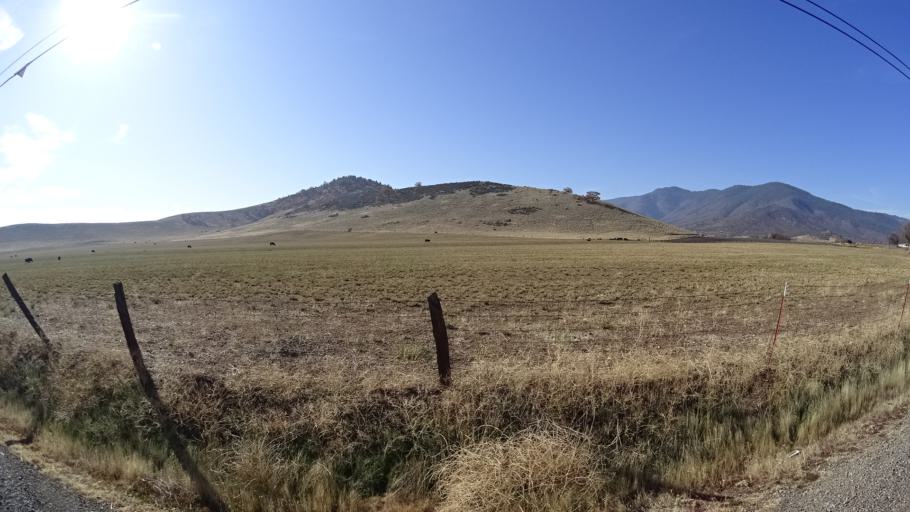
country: US
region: California
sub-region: Siskiyou County
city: Montague
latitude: 41.6510
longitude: -122.5509
